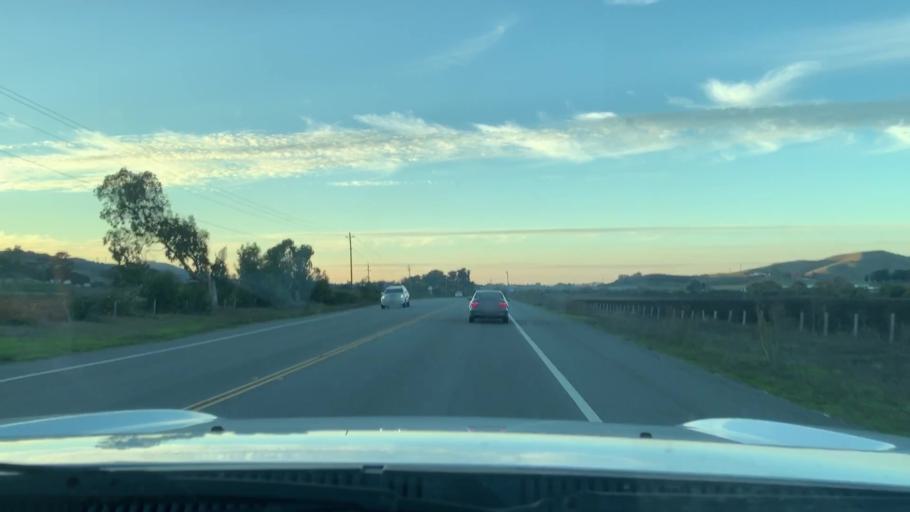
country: US
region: California
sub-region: San Luis Obispo County
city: Los Osos
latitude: 35.2944
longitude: -120.7598
